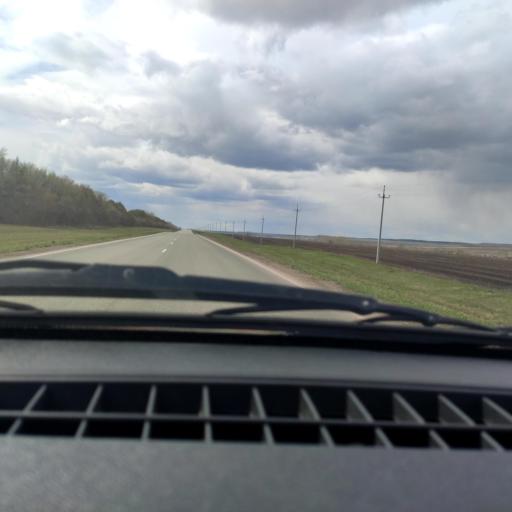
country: RU
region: Bashkortostan
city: Chekmagush
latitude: 55.1106
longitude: 54.9257
